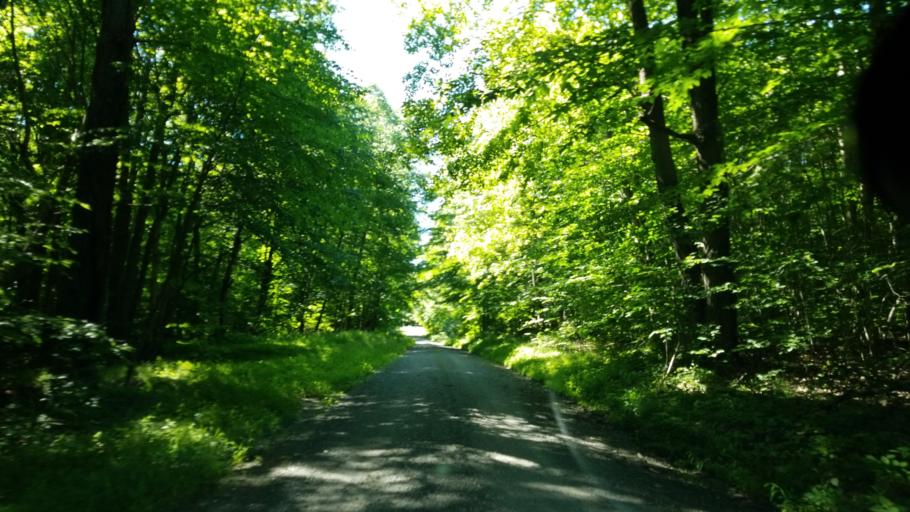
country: US
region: Pennsylvania
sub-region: Clearfield County
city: Clearfield
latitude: 41.2109
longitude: -78.3901
